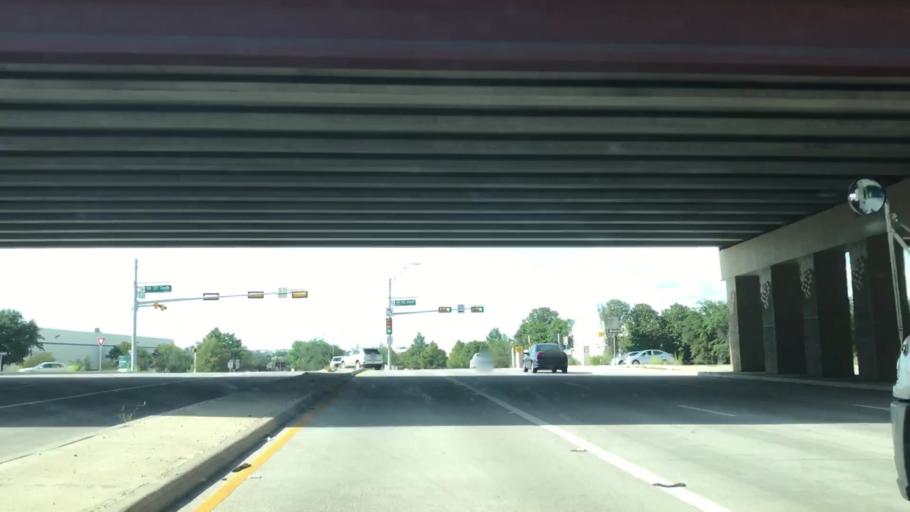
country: US
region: Texas
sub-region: Dallas County
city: Coppell
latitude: 32.9805
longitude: -97.0204
